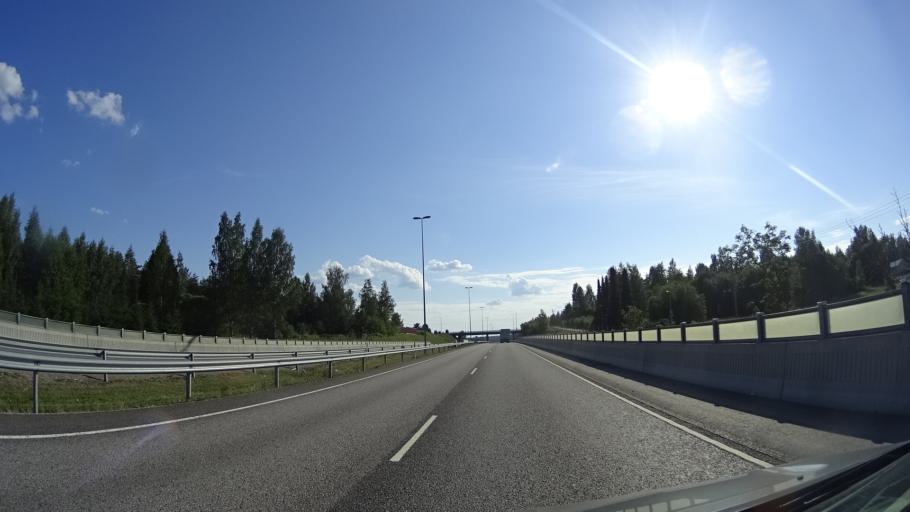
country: FI
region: South Karelia
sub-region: Imatra
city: Imatra
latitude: 61.1746
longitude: 28.7052
